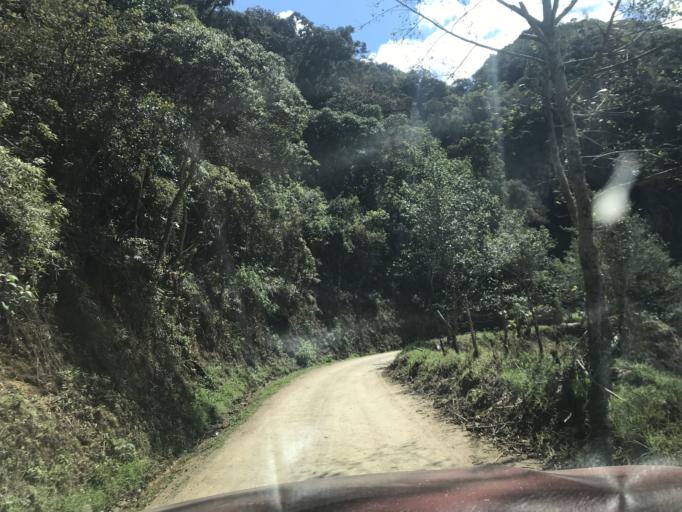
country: PE
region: Cajamarca
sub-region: Provincia de Chota
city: Querocoto
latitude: -6.3521
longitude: -79.0449
